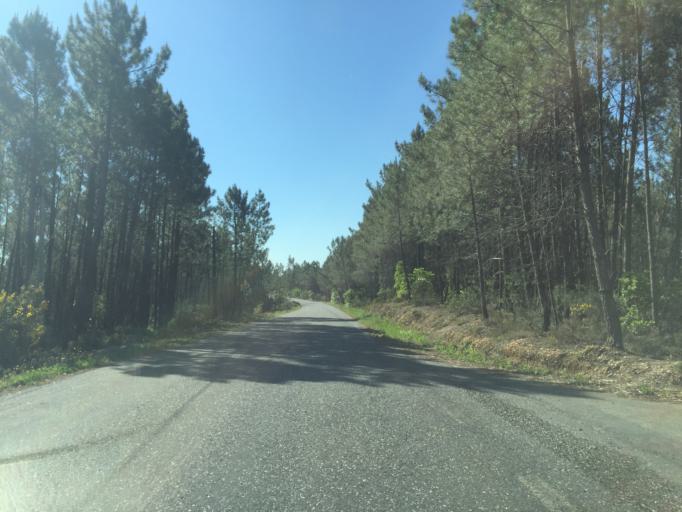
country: PT
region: Coimbra
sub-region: Pampilhosa da Serra
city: Pampilhosa da Serra
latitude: 40.0558
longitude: -7.8509
